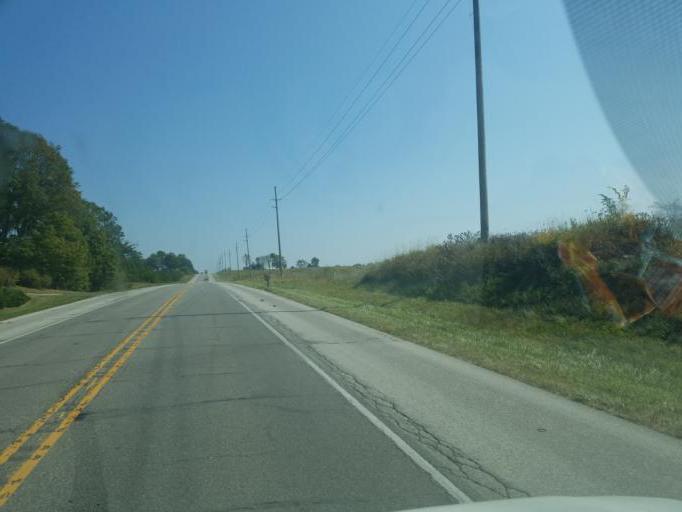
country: US
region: Indiana
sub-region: LaGrange County
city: Lagrange
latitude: 41.6417
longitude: -85.3603
